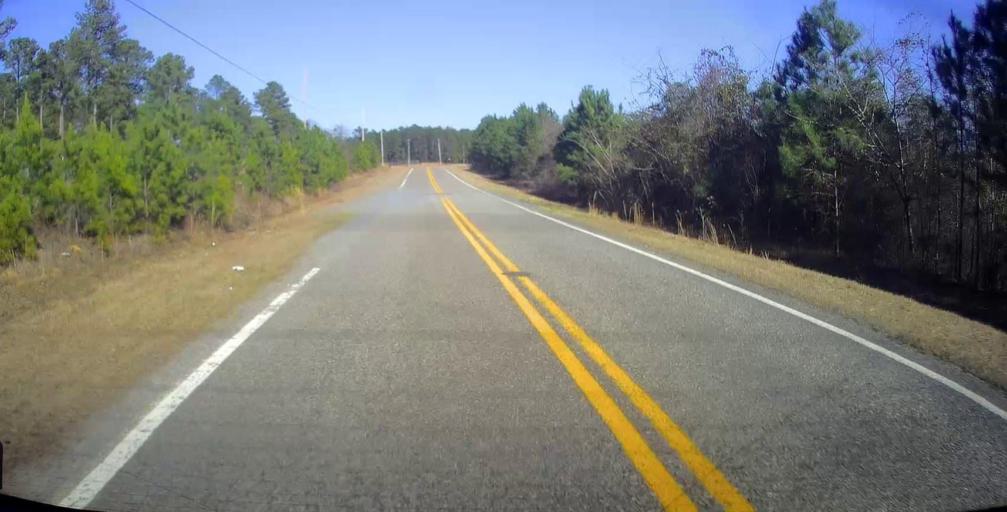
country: US
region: Georgia
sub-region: Peach County
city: Fort Valley
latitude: 32.6357
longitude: -83.9361
